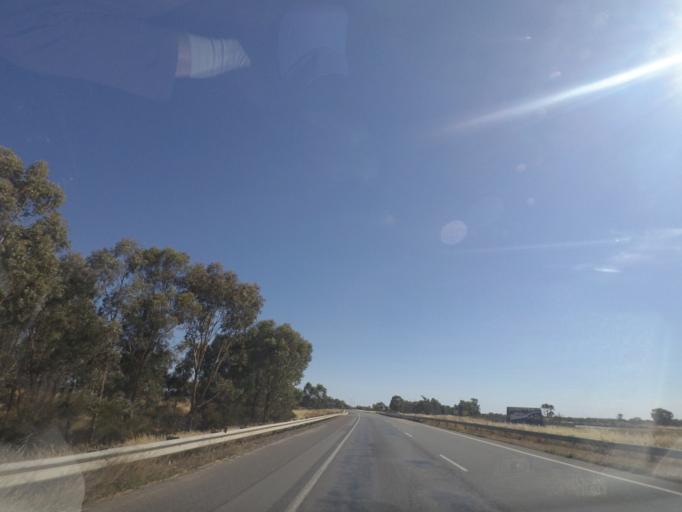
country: AU
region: Victoria
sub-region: Greater Shepparton
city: Shepparton
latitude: -36.7027
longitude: 145.2036
